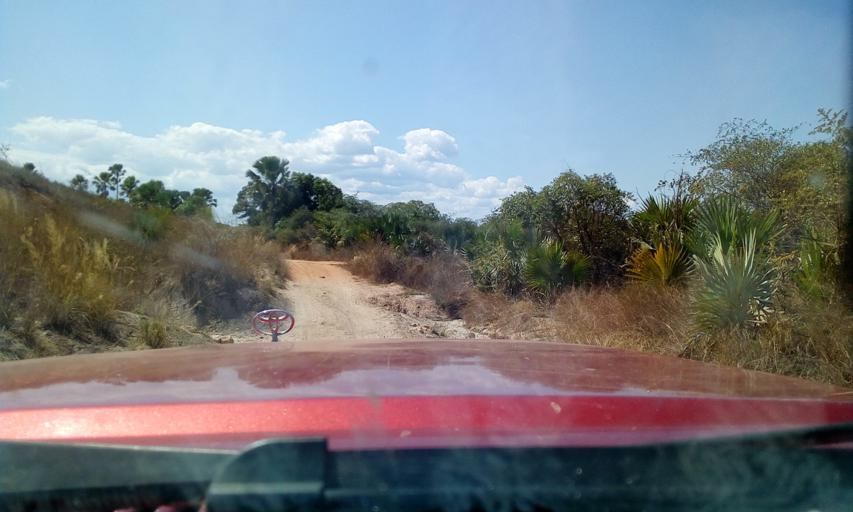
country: MG
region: Boeny
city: Sitampiky
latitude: -16.1284
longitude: 45.5046
